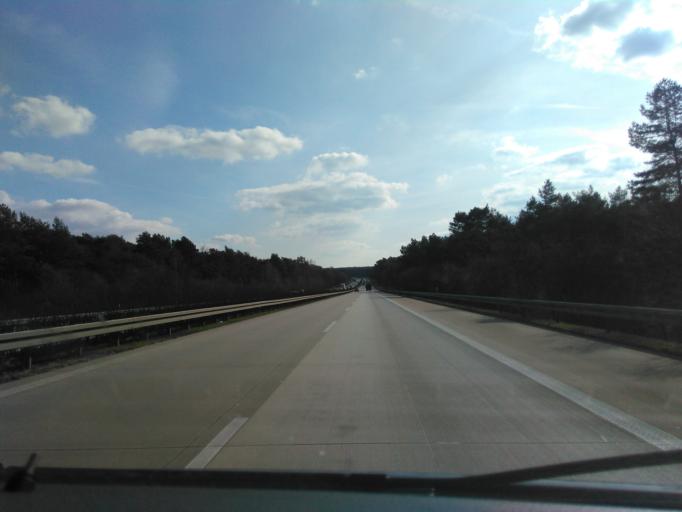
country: DE
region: Brandenburg
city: Bestensee
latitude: 52.2344
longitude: 13.5930
